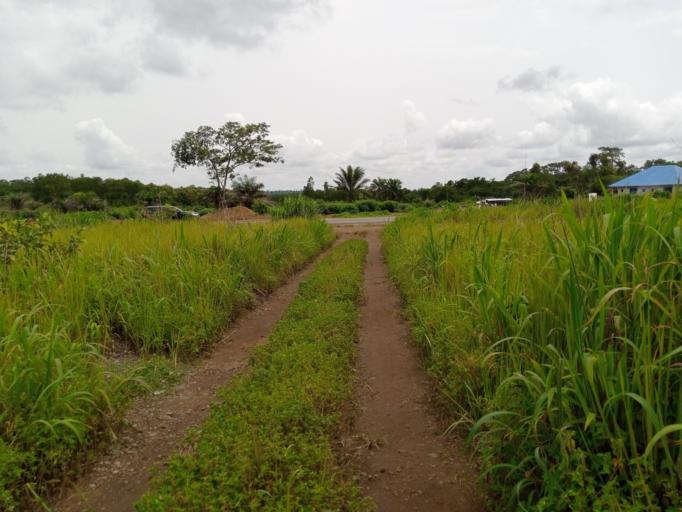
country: SL
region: Southern Province
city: Moyamba
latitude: 8.1706
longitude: -12.4171
